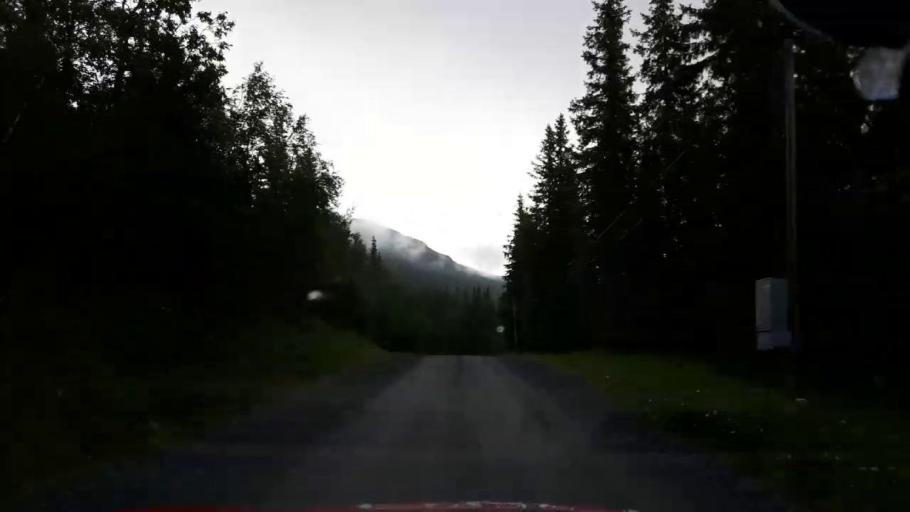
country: NO
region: Nordland
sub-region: Hattfjelldal
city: Hattfjelldal
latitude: 64.8845
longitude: 14.8356
